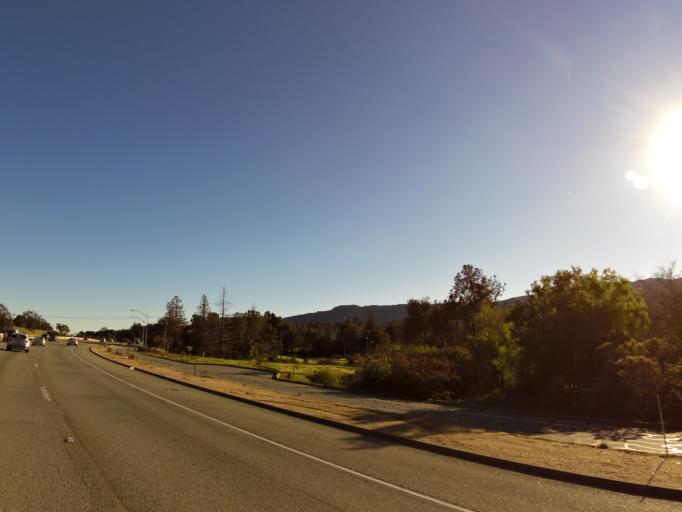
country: US
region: California
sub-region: Santa Clara County
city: Los Altos Hills
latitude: 37.3625
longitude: -122.1215
